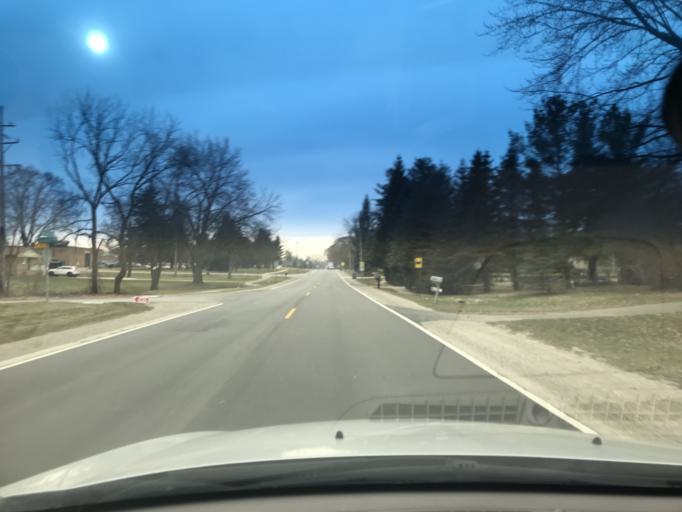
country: US
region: Michigan
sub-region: Macomb County
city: Shelby
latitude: 42.6914
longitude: -83.0544
